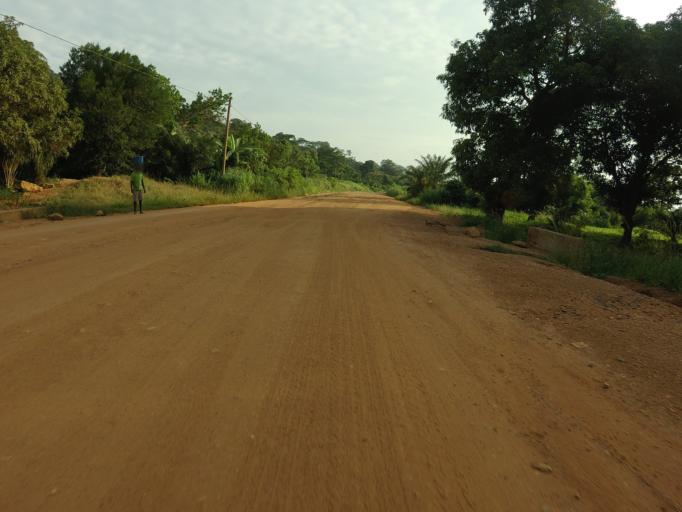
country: TG
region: Plateaux
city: Kpalime
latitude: 6.9154
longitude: 0.4562
